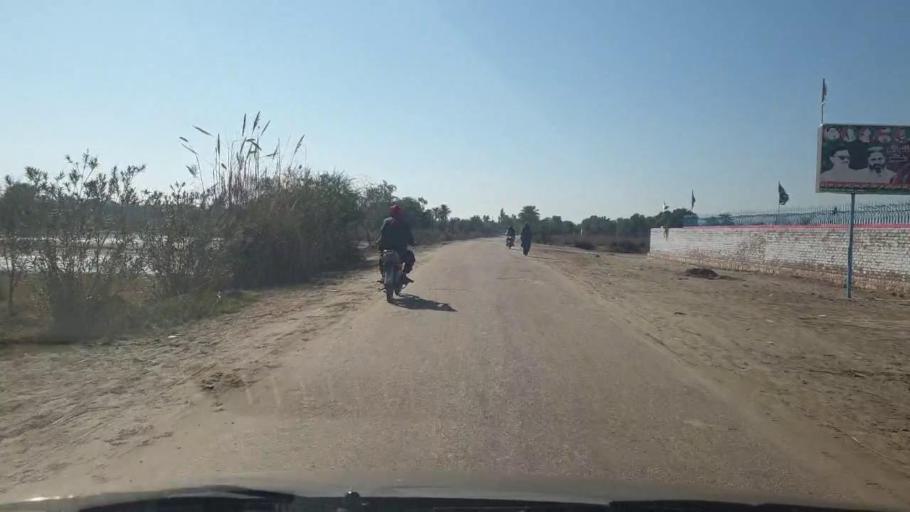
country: PK
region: Sindh
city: Bozdar
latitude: 27.1286
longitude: 68.6345
